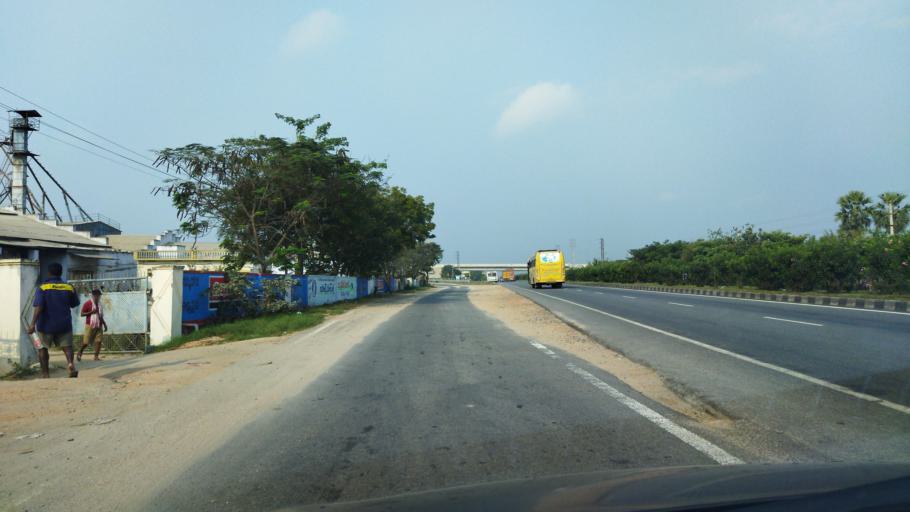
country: IN
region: Telangana
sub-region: Nalgonda
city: Nalgonda
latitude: 17.1682
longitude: 79.3985
